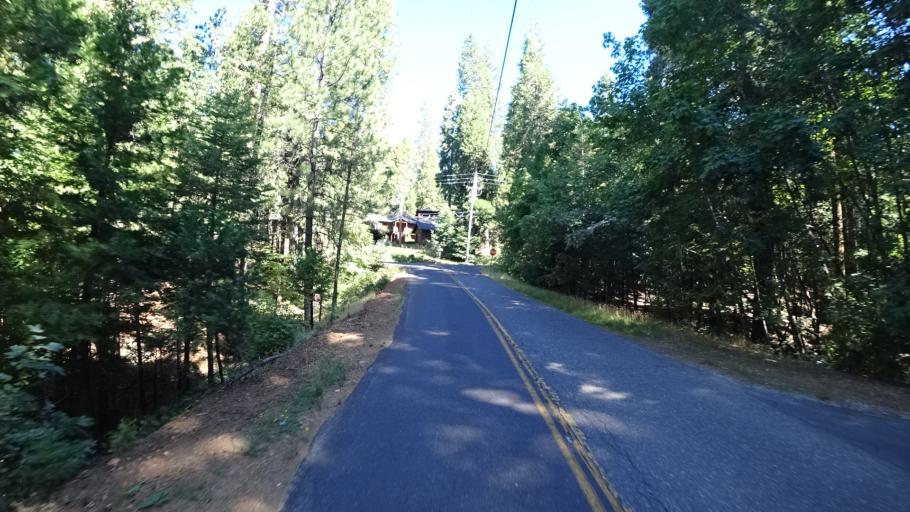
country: US
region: California
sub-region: Calaveras County
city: Arnold
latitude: 38.2594
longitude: -120.3236
